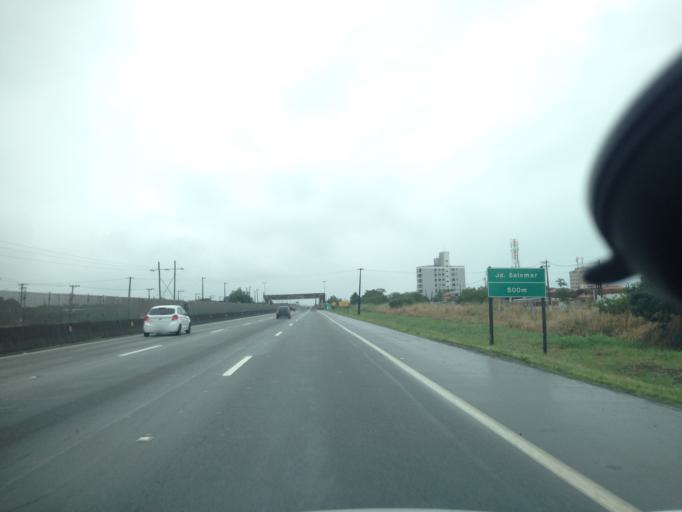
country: BR
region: Sao Paulo
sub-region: Mongagua
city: Mongagua
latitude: -24.0793
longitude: -46.5948
